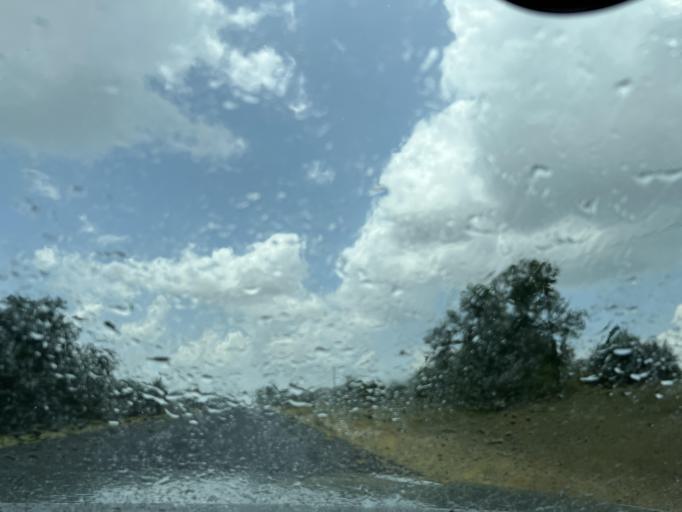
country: US
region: Texas
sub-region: Wise County
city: Boyd
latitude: 33.1169
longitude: -97.6551
